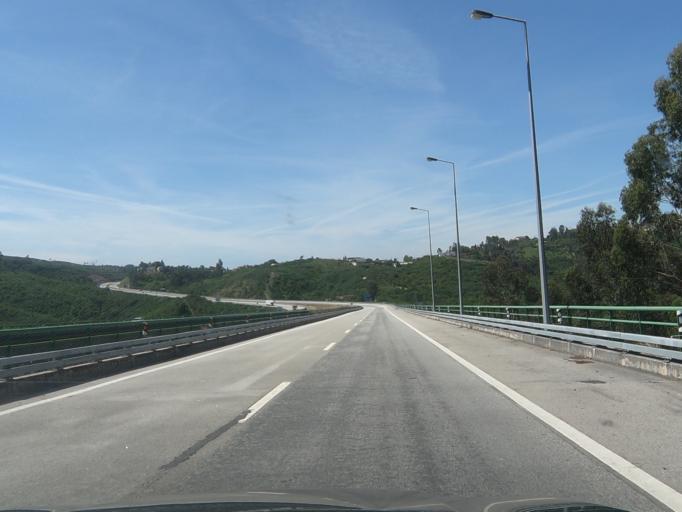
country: PT
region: Viseu
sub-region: Castro Daire
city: Castro Daire
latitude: 40.8914
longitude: -7.9188
